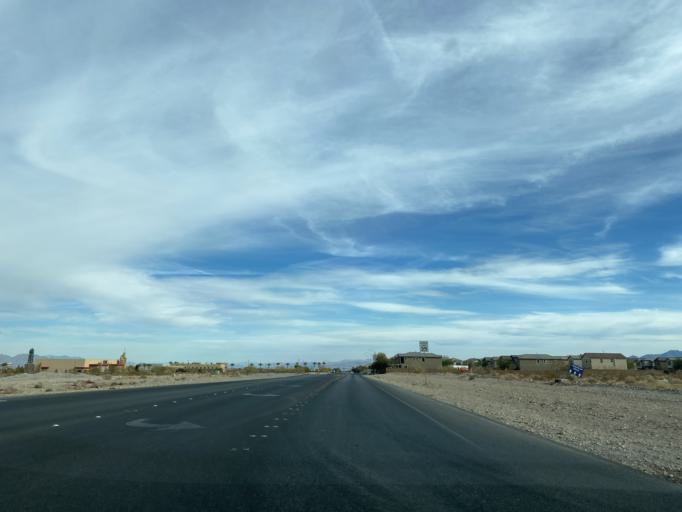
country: US
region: Nevada
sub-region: Clark County
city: Enterprise
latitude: 36.0409
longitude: -115.2702
